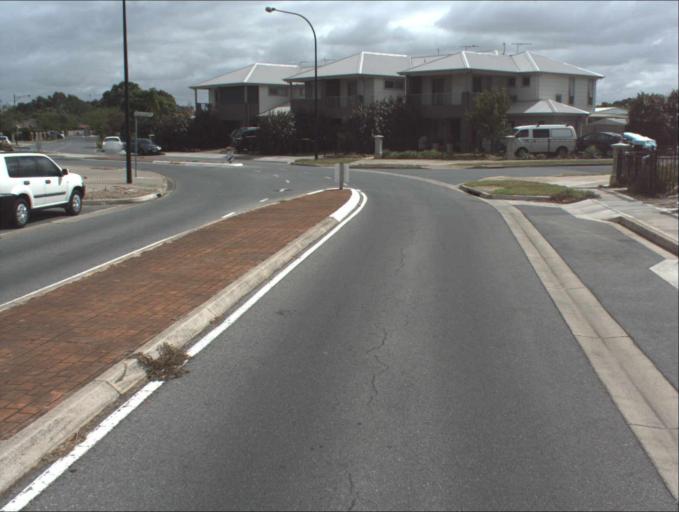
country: AU
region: South Australia
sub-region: Charles Sturt
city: Woodville
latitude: -34.8705
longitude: 138.5622
